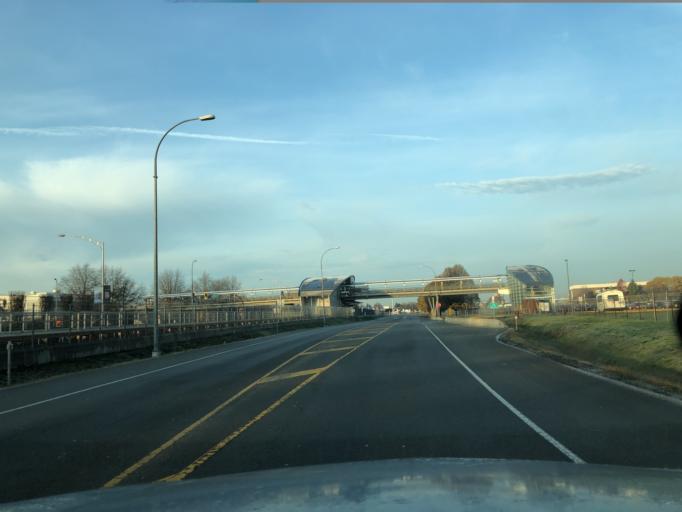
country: CA
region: British Columbia
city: Richmond
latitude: 49.1933
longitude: -123.1555
